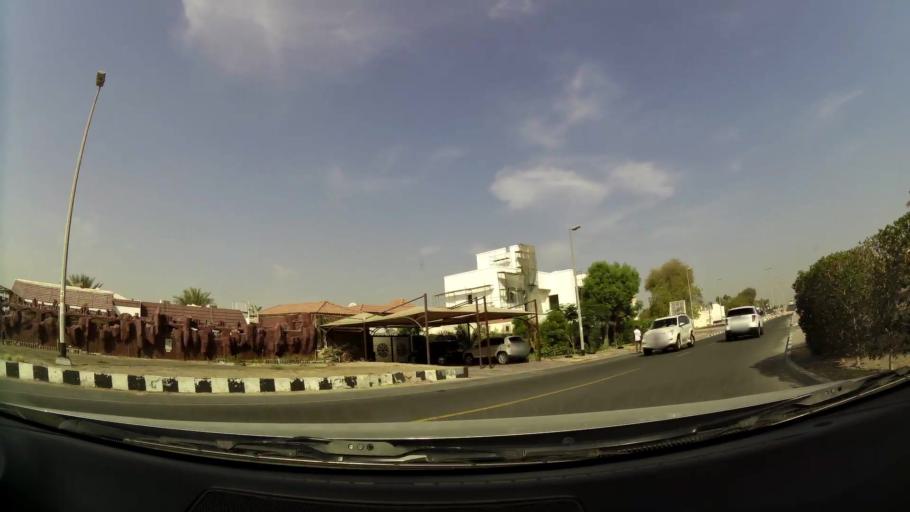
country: AE
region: Ash Shariqah
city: Sharjah
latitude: 25.2259
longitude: 55.3994
